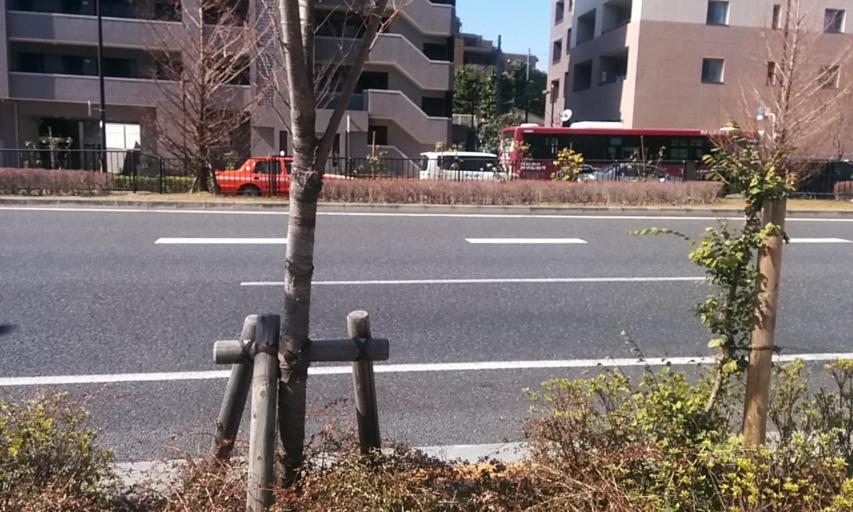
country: JP
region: Tokyo
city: Tokyo
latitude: 35.6766
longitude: 139.6881
